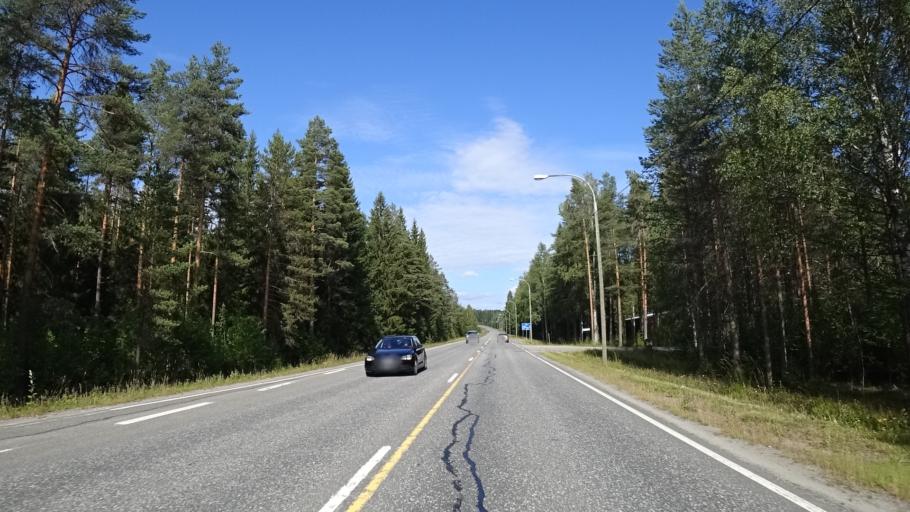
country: FI
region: North Karelia
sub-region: Joensuu
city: Eno
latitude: 62.7757
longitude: 30.0595
